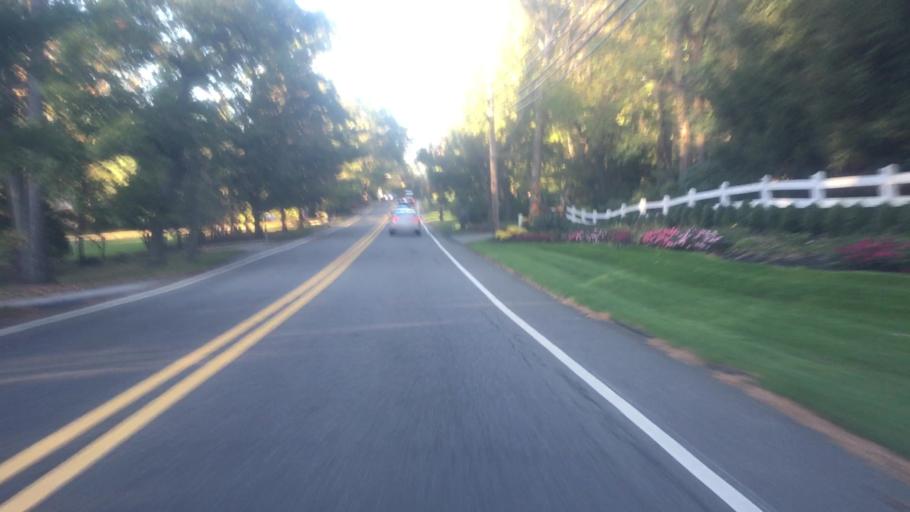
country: US
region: New Jersey
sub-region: Bergen County
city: Franklin Lakes
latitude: 40.9982
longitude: -74.1973
